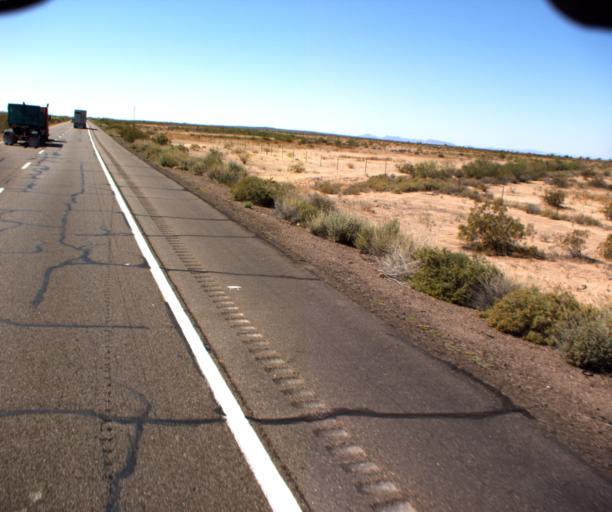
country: US
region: Arizona
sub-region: Maricopa County
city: Gila Bend
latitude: 32.8624
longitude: -113.1740
